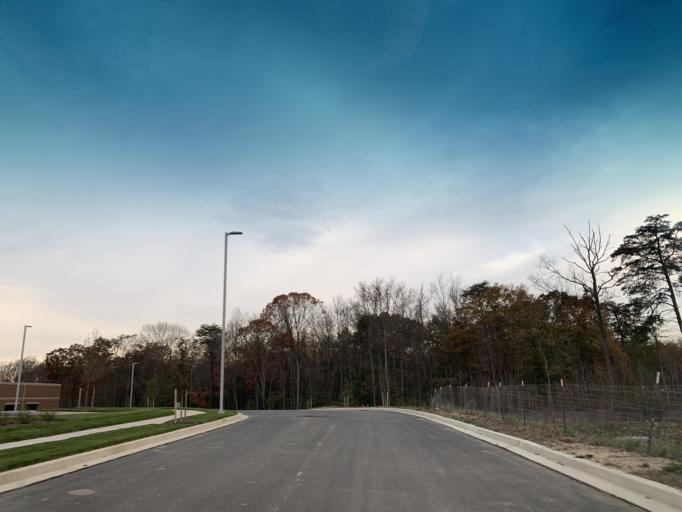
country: US
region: Maryland
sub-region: Baltimore County
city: Bowleys Quarters
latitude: 39.3495
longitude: -76.4149
